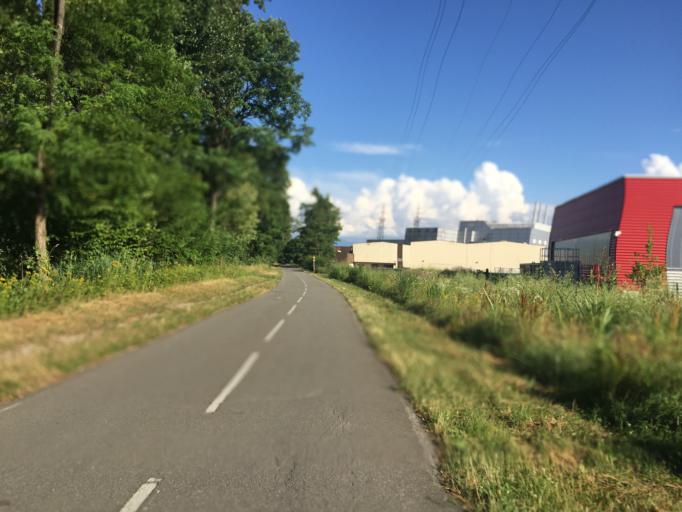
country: FR
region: Rhone-Alpes
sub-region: Departement de la Savoie
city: La Motte-Servolex
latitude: 45.5939
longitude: 5.8937
